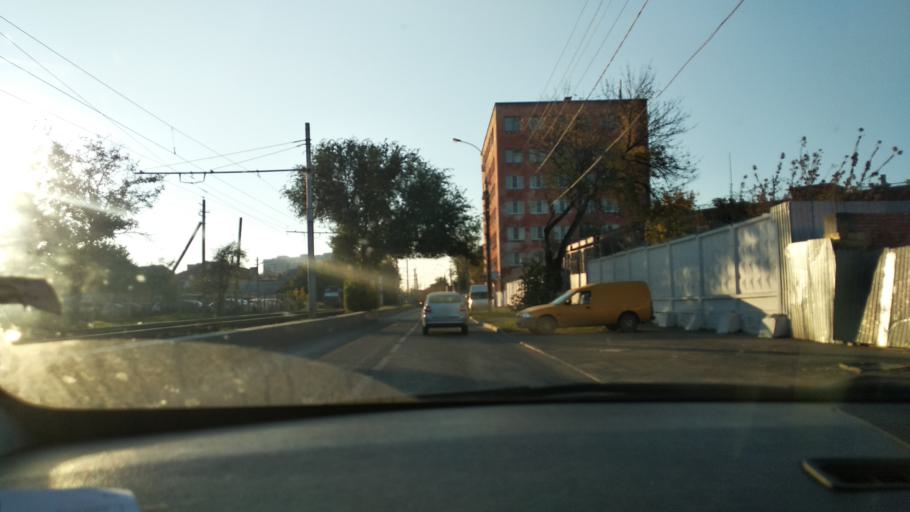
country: RU
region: Krasnodarskiy
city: Krasnodar
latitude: 45.0091
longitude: 39.0143
